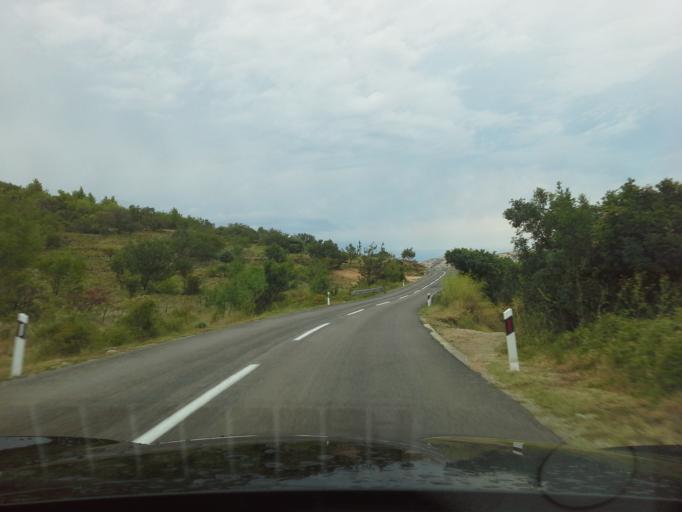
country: HR
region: Primorsko-Goranska
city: Banjol
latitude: 44.7143
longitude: 14.8277
